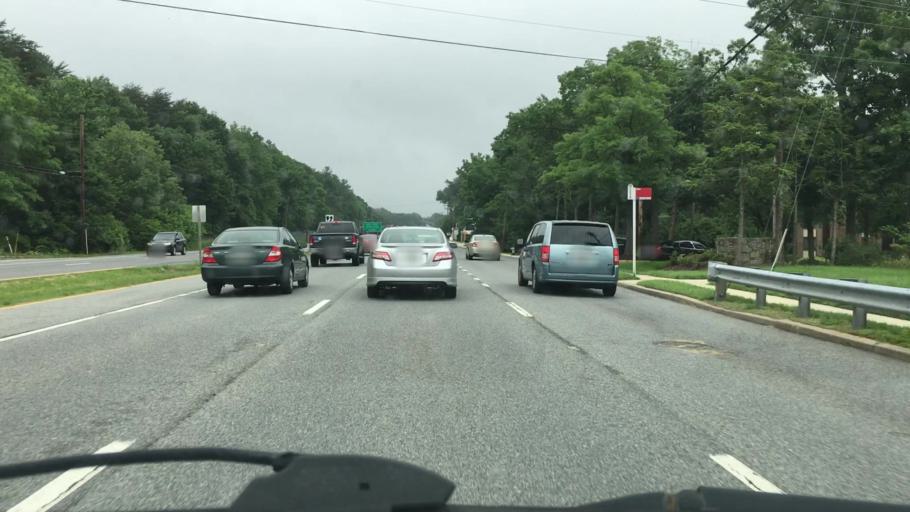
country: US
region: Maryland
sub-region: Prince George's County
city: Goddard
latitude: 38.9914
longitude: -76.8605
